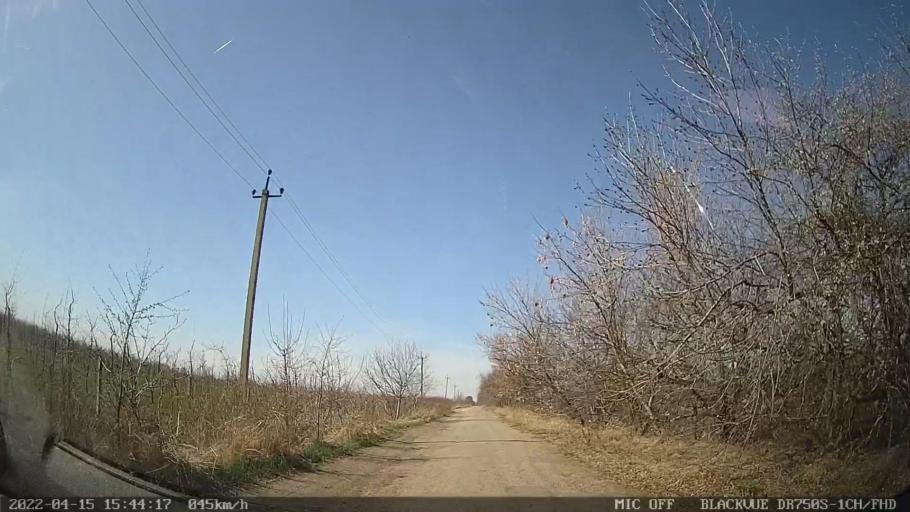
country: MD
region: Raionul Ocnita
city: Otaci
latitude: 48.3696
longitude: 27.9230
